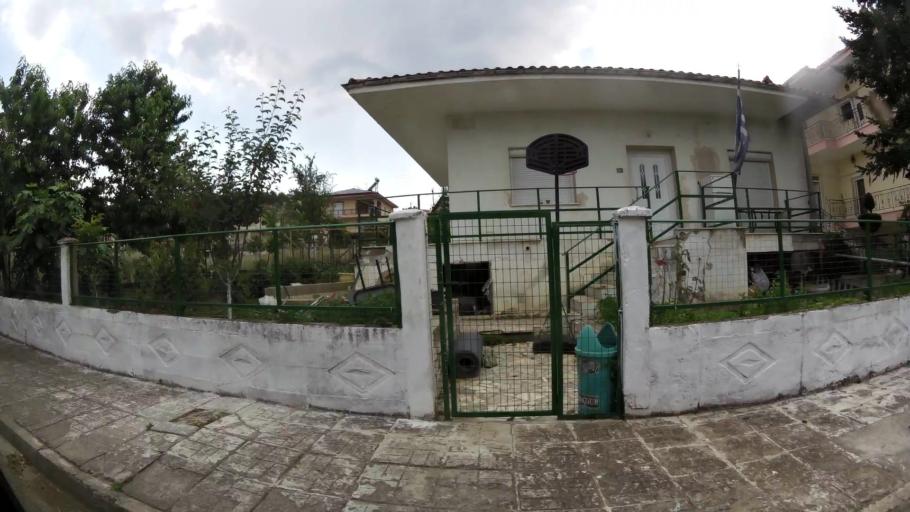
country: GR
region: West Macedonia
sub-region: Nomos Kozanis
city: Koila
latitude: 40.3260
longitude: 21.8264
